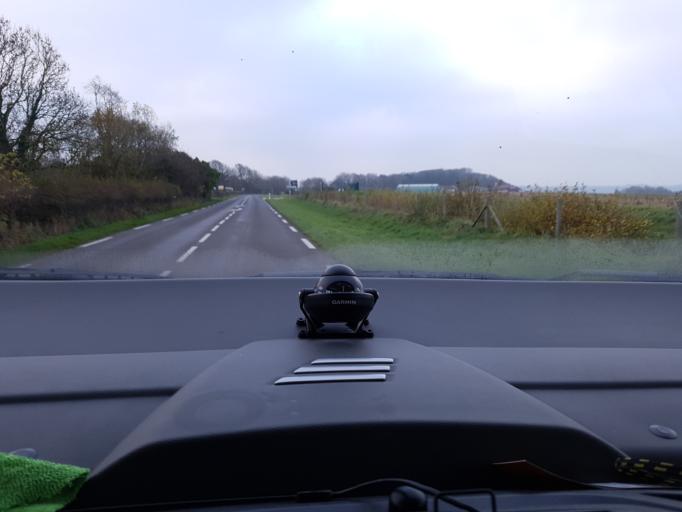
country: FR
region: Haute-Normandie
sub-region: Departement de la Seine-Maritime
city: Eu
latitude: 50.0711
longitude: 1.4321
